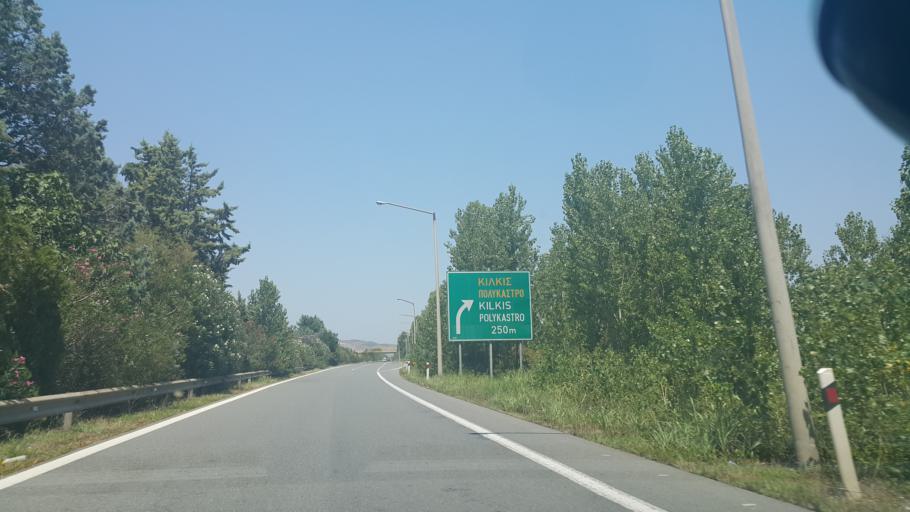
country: GR
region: Central Macedonia
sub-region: Nomos Kilkis
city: Polykastro
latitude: 40.9853
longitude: 22.6051
